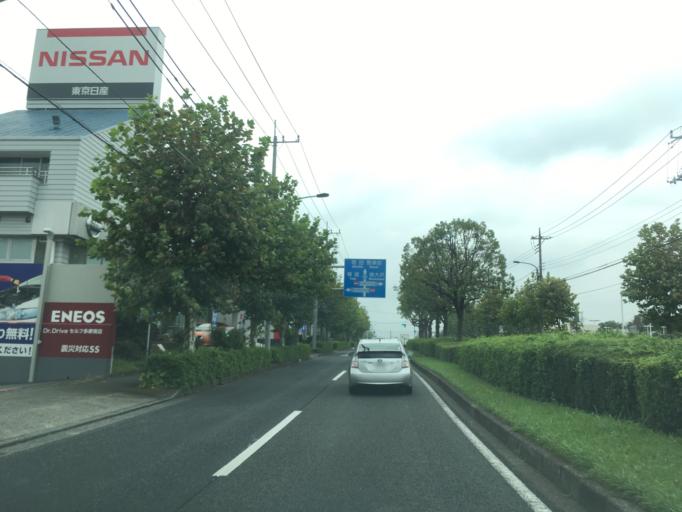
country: JP
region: Tokyo
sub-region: Machida-shi
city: Machida
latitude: 35.6130
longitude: 139.4429
